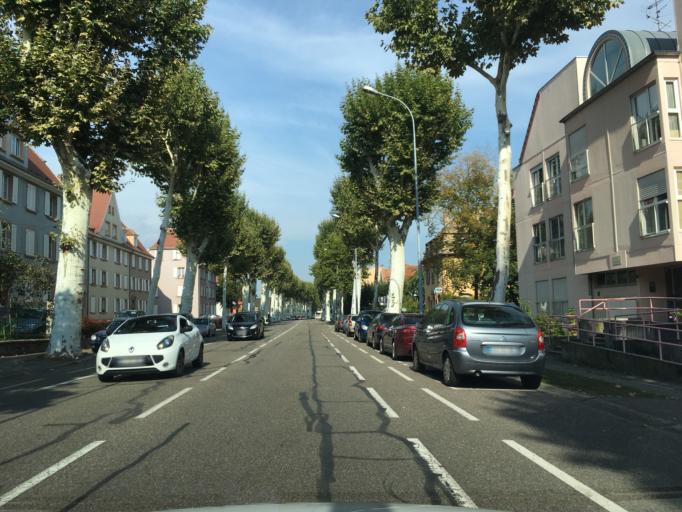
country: FR
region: Alsace
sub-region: Departement du Haut-Rhin
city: Colmar
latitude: 48.0859
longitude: 7.3674
